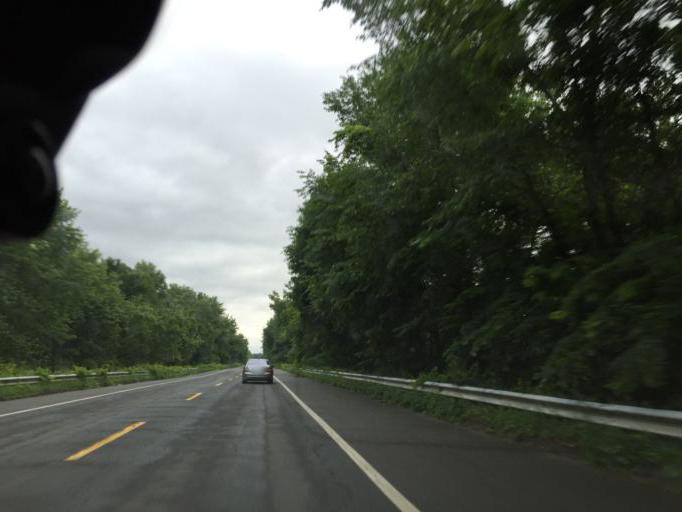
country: US
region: Connecticut
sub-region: Litchfield County
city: Canaan
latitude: 42.0710
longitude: -73.3310
